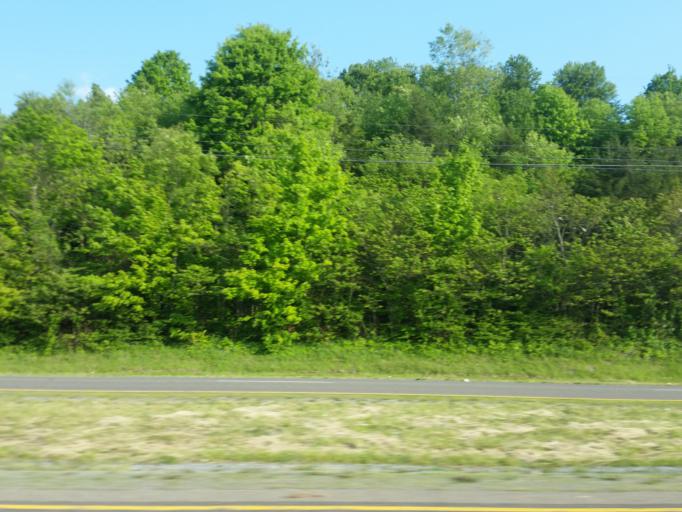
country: US
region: Virginia
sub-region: Tazewell County
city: Claypool Hill
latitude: 37.0033
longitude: -81.8103
